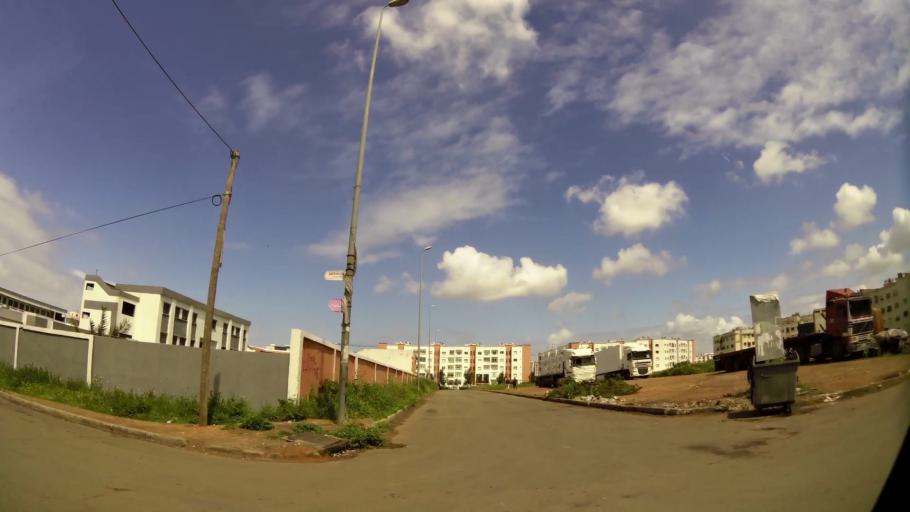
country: MA
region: Grand Casablanca
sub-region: Mediouna
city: Tit Mellil
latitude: 33.6054
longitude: -7.4843
